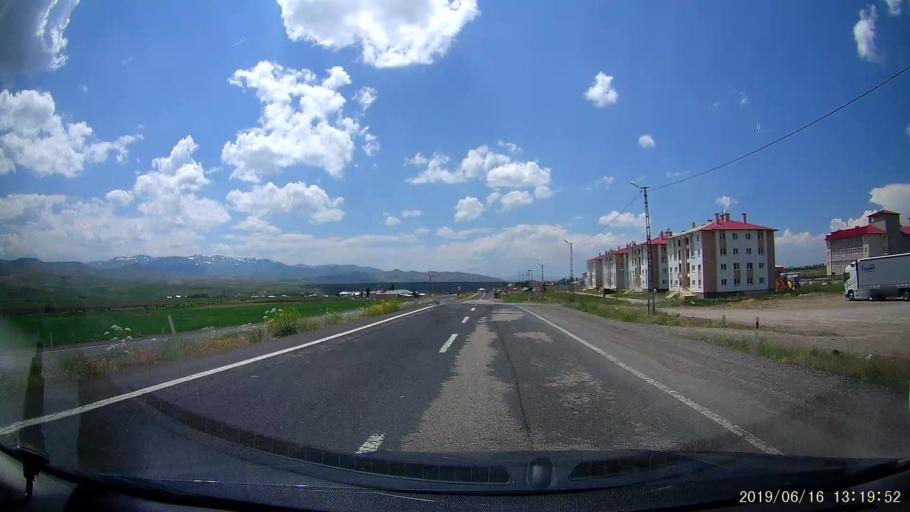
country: TR
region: Agri
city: Taslicay
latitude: 39.6327
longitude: 43.3977
